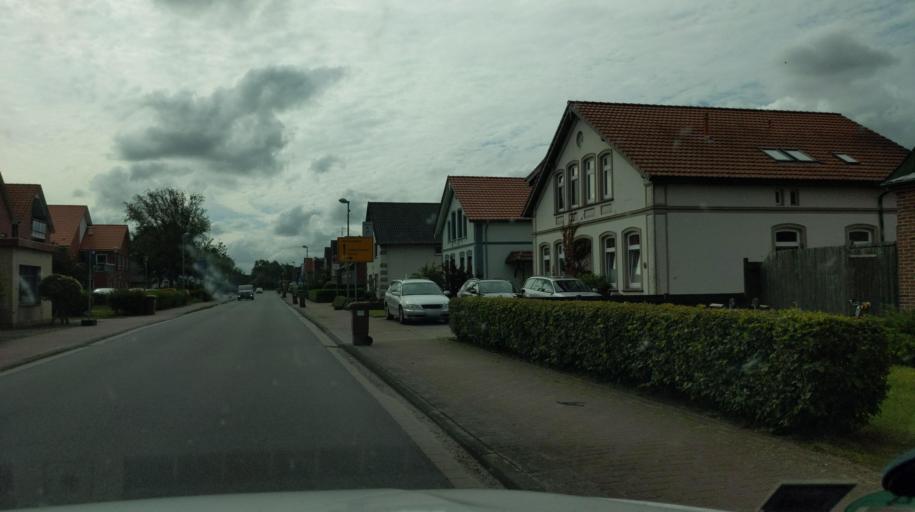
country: DE
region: Lower Saxony
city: Butjadingen
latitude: 53.5729
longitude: 8.3650
